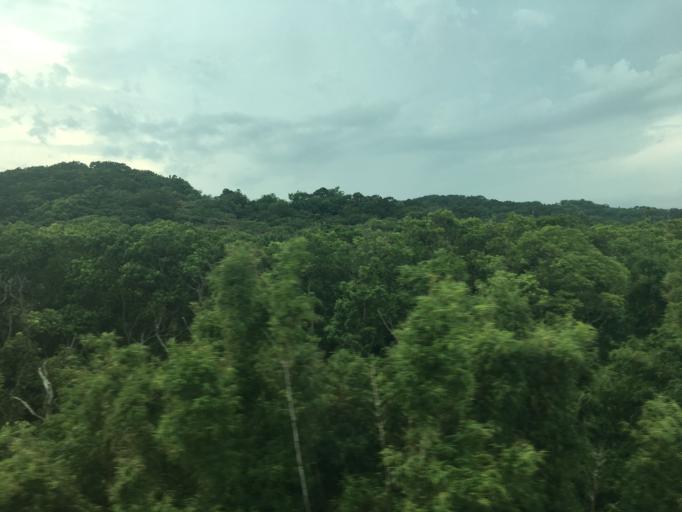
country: TW
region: Taiwan
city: Taoyuan City
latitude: 25.0791
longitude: 121.3069
